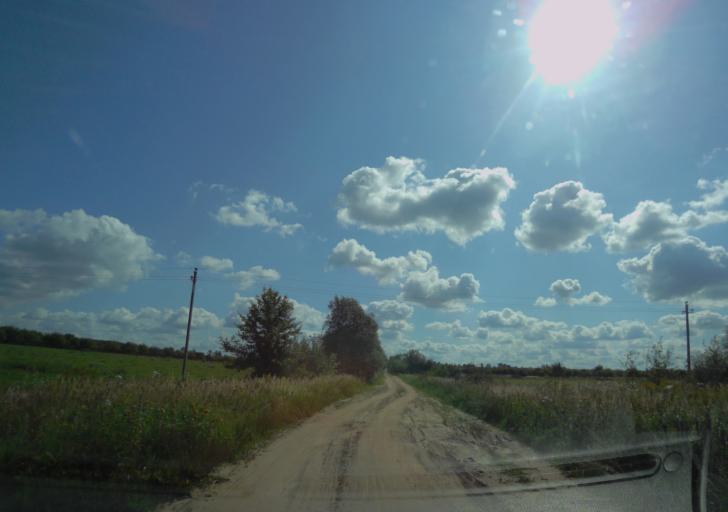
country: BY
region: Minsk
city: Zyembin
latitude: 54.4143
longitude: 28.3749
